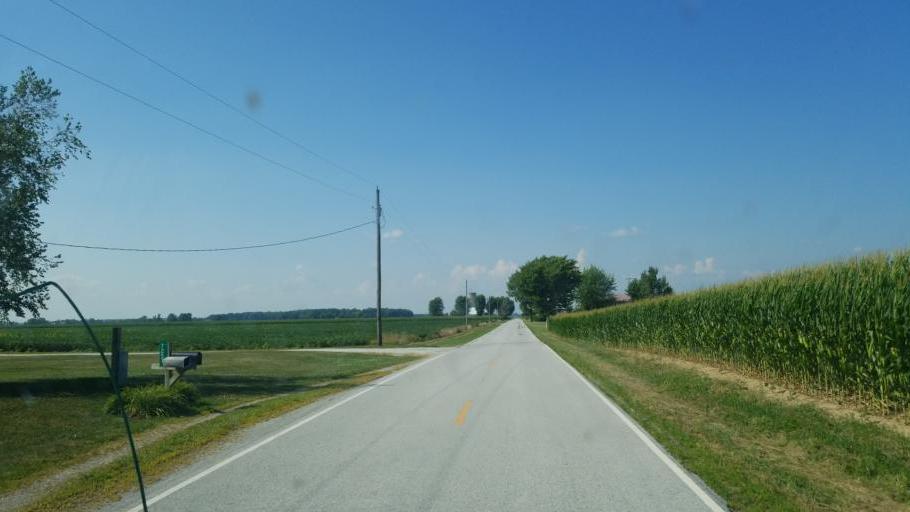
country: US
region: Ohio
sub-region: Hardin County
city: Forest
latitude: 40.7124
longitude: -83.4958
